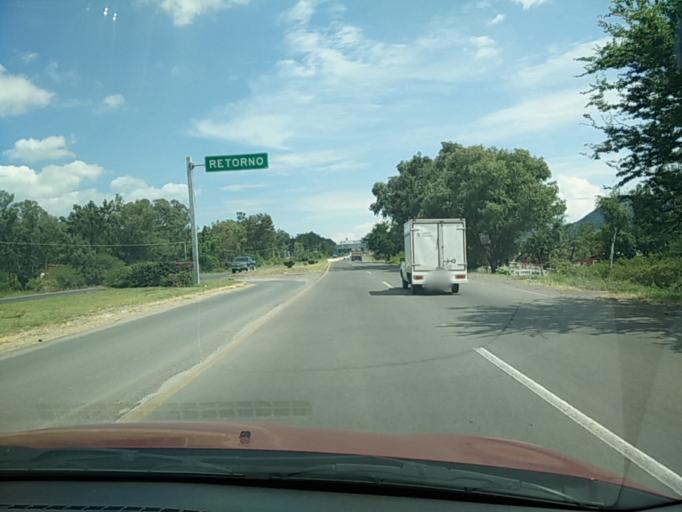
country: MX
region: Jalisco
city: Ixtlahuacan de los Membrillos
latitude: 20.3656
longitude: -103.2065
